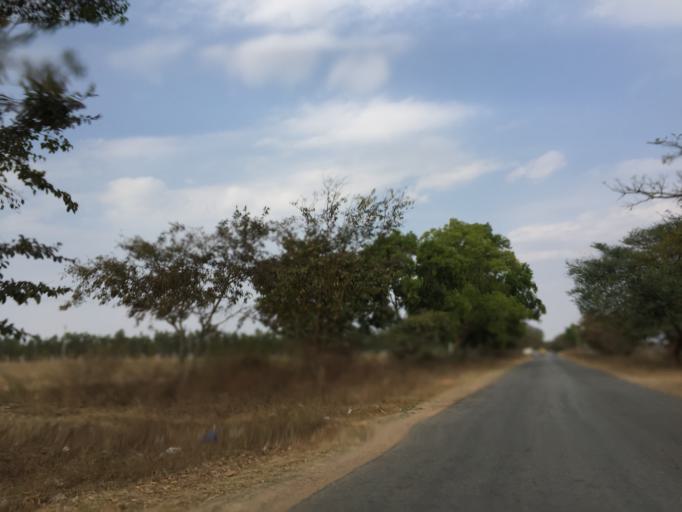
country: IN
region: Karnataka
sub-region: Chikkaballapur
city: Chik Ballapur
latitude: 13.4078
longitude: 77.7132
